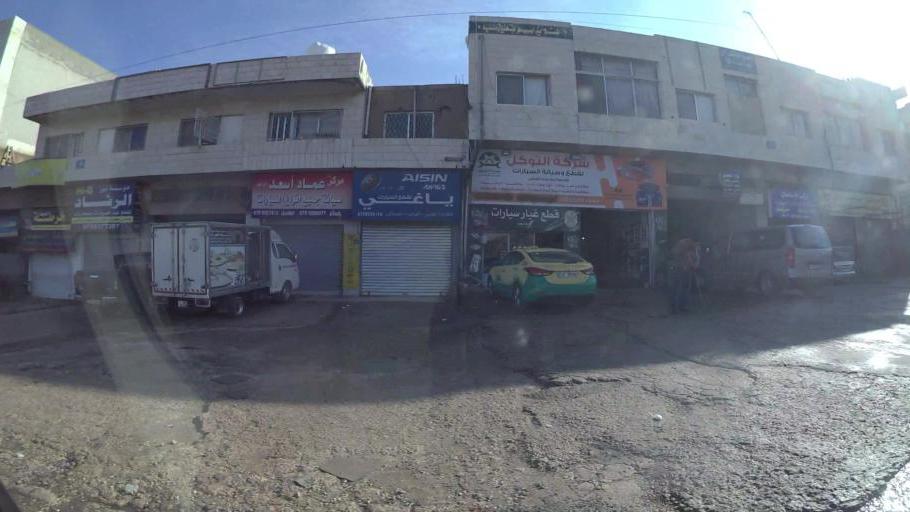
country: JO
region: Amman
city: Al Jubayhah
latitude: 32.0145
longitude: 35.8488
